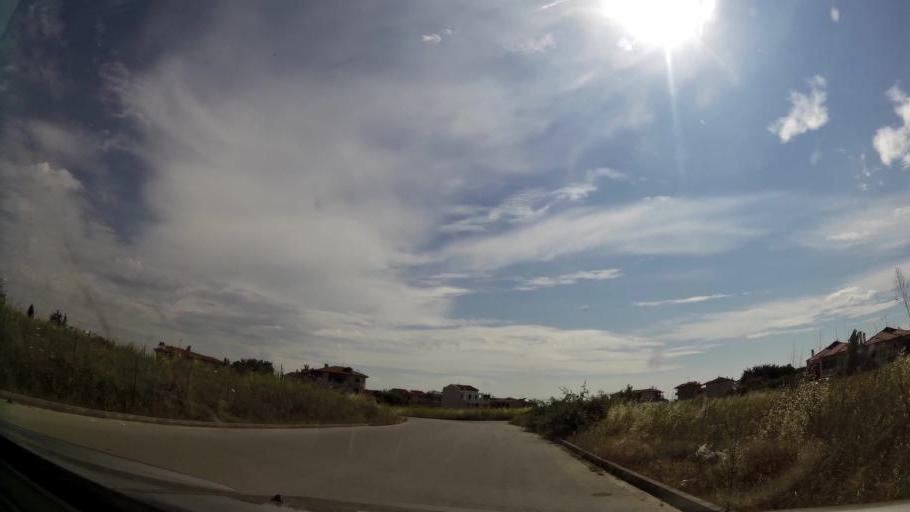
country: GR
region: Central Macedonia
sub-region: Nomos Pierias
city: Katerini
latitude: 40.2777
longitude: 22.4847
